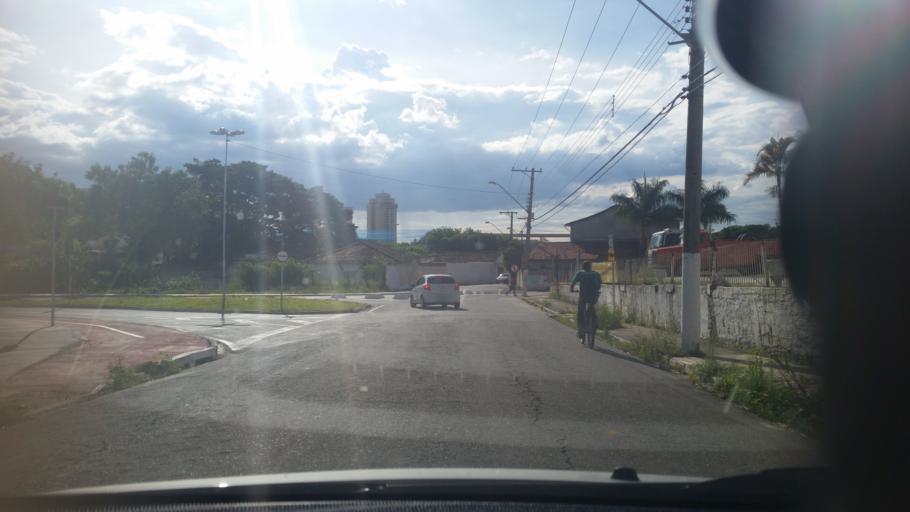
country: BR
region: Sao Paulo
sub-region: Taubate
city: Taubate
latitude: -23.0229
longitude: -45.5731
